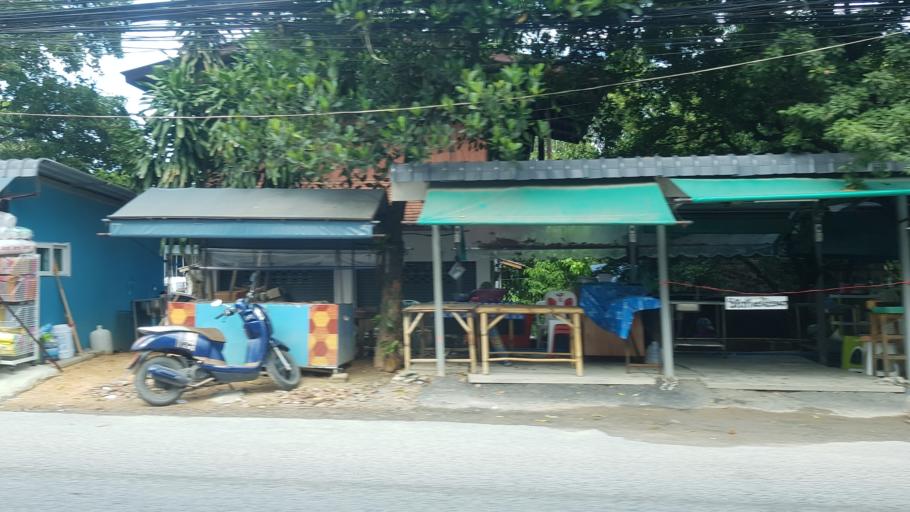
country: TH
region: Surat Thani
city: Ko Samui
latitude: 9.5315
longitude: 100.0437
